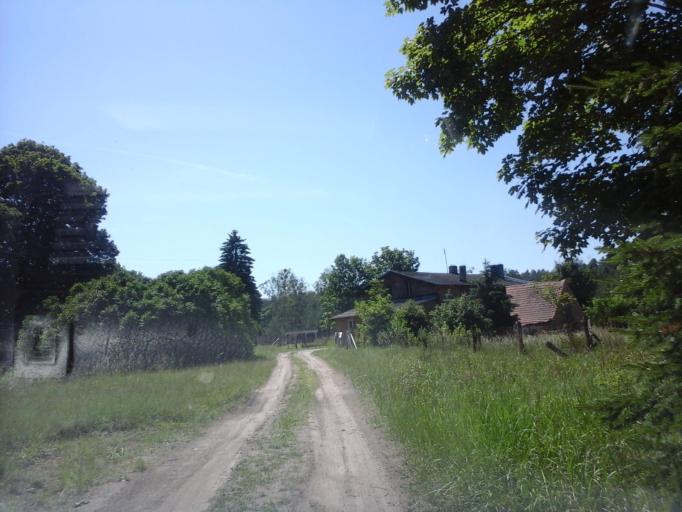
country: PL
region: West Pomeranian Voivodeship
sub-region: Powiat drawski
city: Kalisz Pomorski
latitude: 53.1100
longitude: 15.9268
